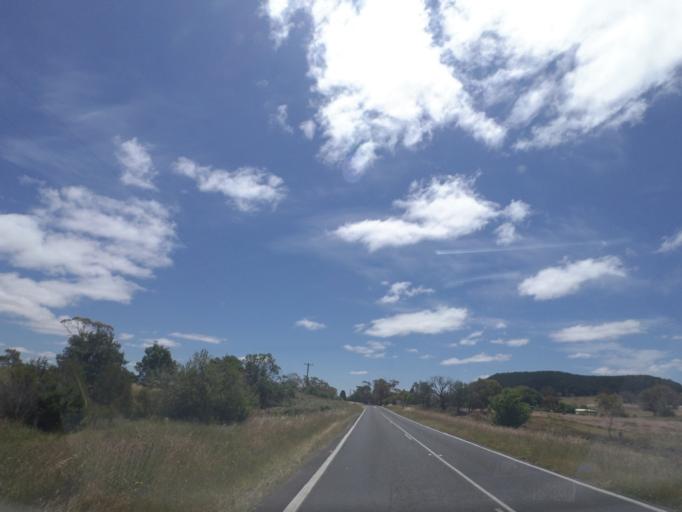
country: AU
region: Victoria
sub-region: Mount Alexander
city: Castlemaine
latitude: -37.2795
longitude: 144.1504
